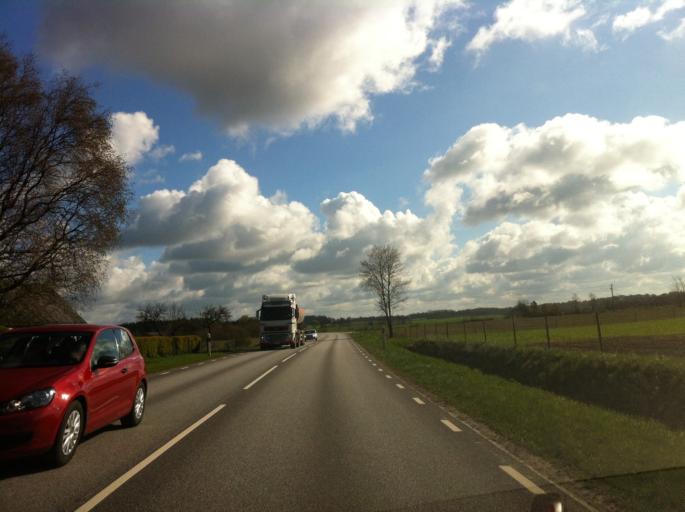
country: SE
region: Skane
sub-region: Eslovs Kommun
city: Stehag
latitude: 55.8998
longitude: 13.3287
